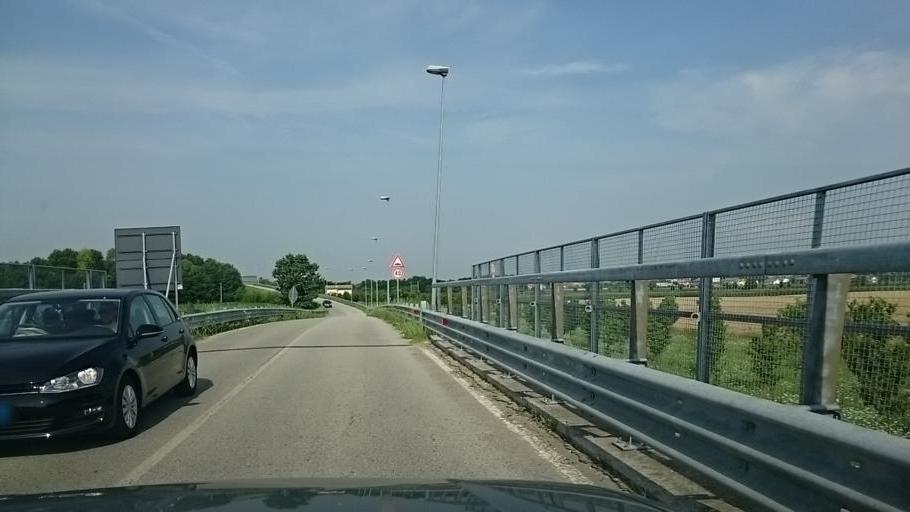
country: IT
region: Veneto
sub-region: Provincia di Treviso
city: Castelfranco Veneto
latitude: 45.6507
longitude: 11.9226
